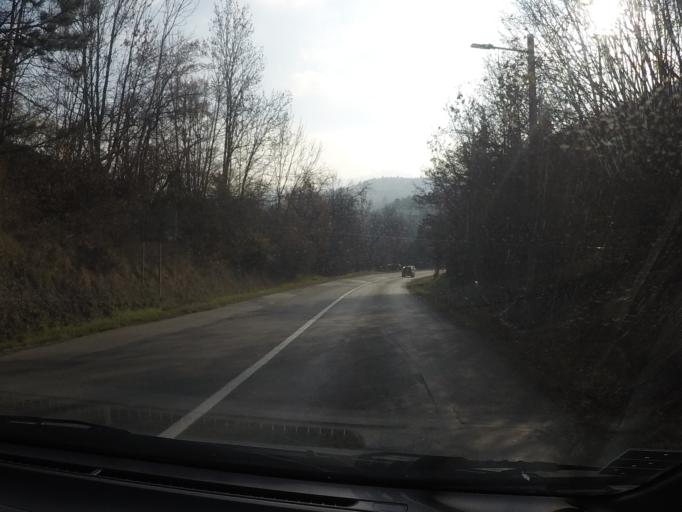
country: SK
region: Banskobystricky
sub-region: Okres Banska Bystrica
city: Banska Stiavnica
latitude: 48.4667
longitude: 18.9028
